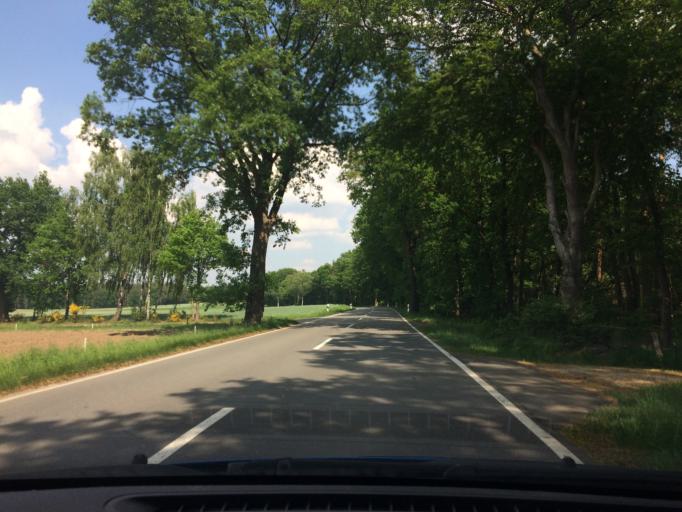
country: DE
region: Lower Saxony
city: Neu Darchau
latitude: 53.2196
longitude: 10.8585
